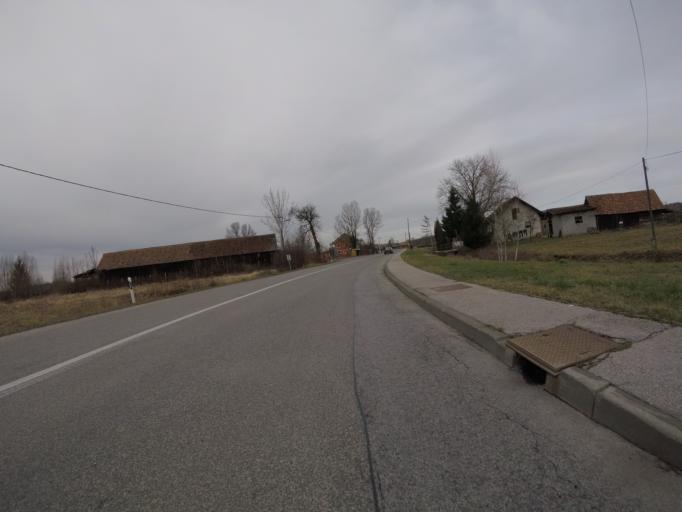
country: HR
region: Grad Zagreb
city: Horvati
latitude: 45.5750
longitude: 15.8608
